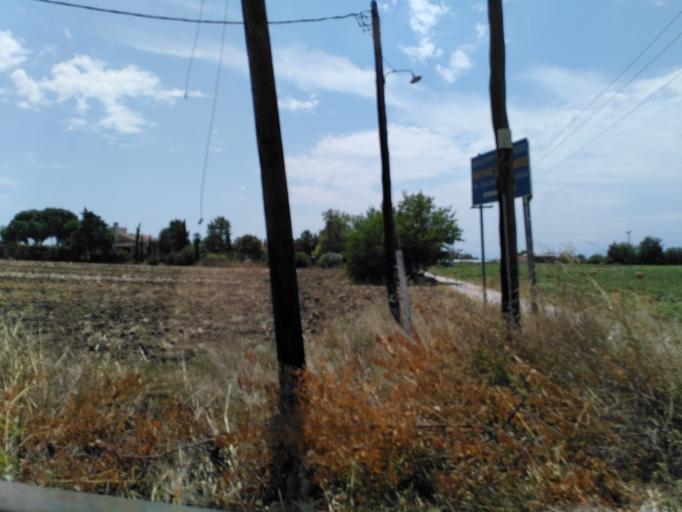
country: GR
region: Central Macedonia
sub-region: Nomos Thessalonikis
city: Epanomi
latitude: 40.4316
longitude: 22.9172
